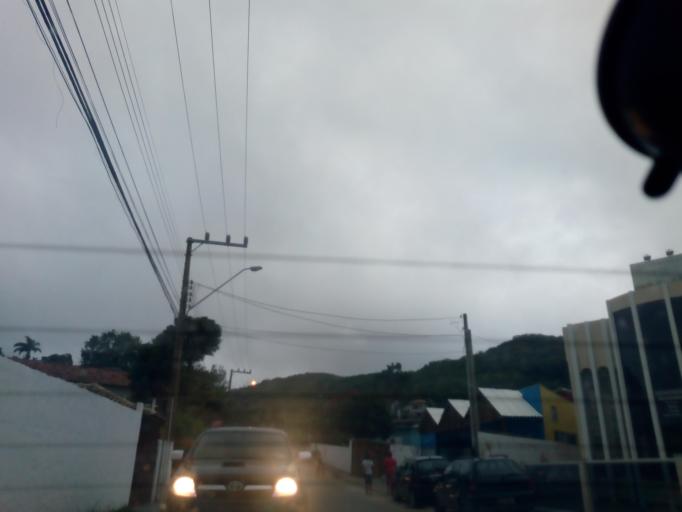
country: BR
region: Santa Catarina
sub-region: Florianopolis
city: Itacorubi
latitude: -27.3948
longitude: -48.4239
